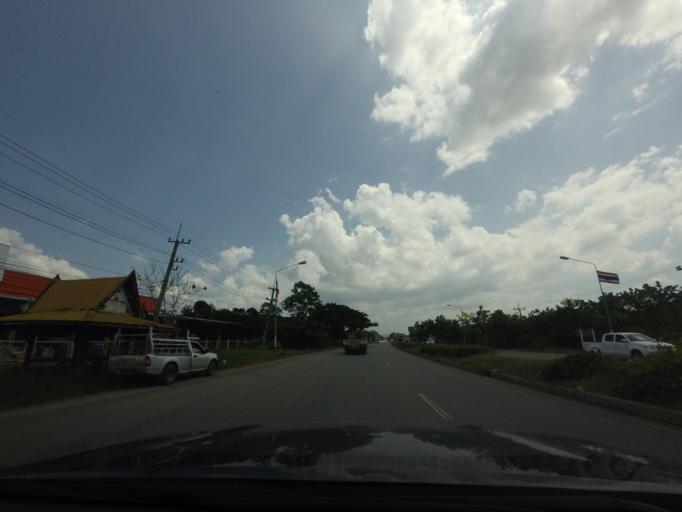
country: TH
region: Phetchabun
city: Phetchabun
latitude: 16.2482
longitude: 101.0709
